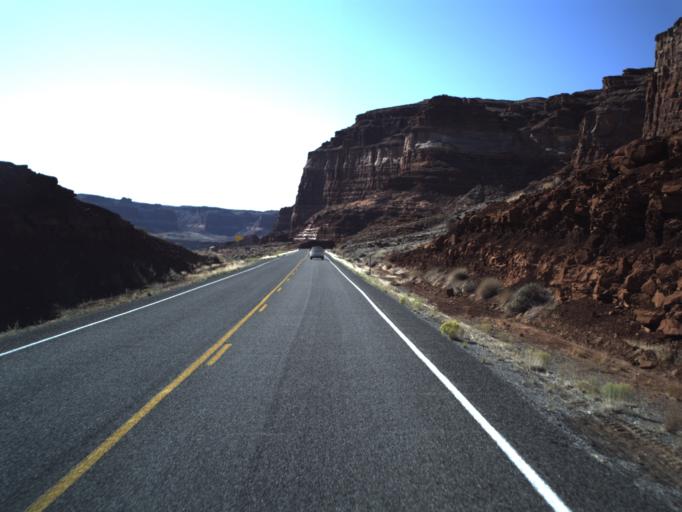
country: US
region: Utah
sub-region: San Juan County
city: Blanding
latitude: 37.9068
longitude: -110.4006
